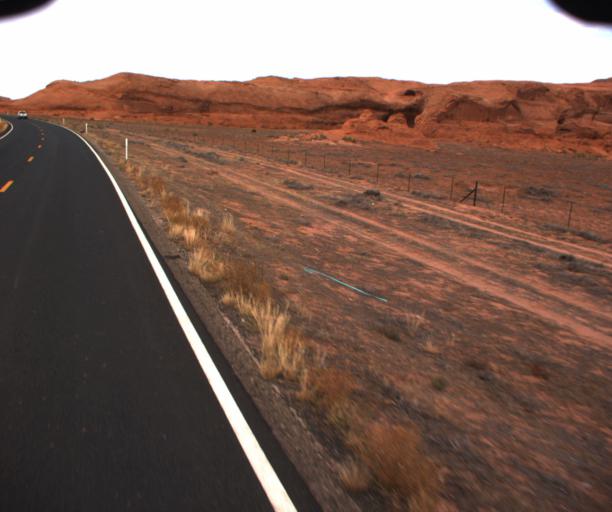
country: US
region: Arizona
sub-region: Apache County
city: Many Farms
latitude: 36.7643
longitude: -109.6523
